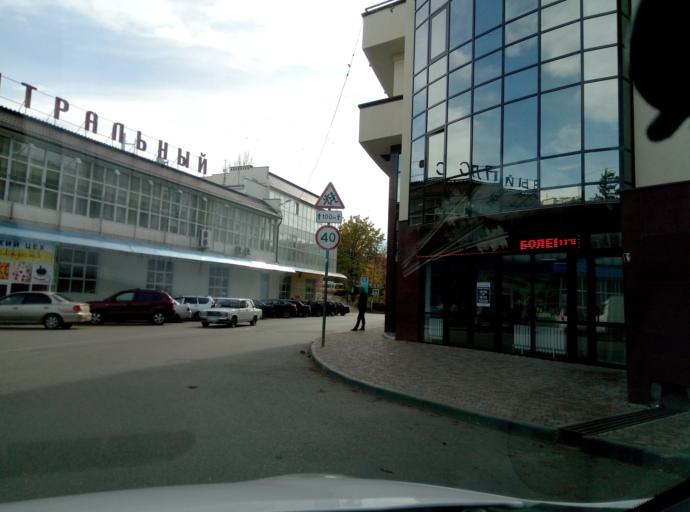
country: RU
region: Stavropol'skiy
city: Kislovodsk
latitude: 43.9089
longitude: 42.7081
